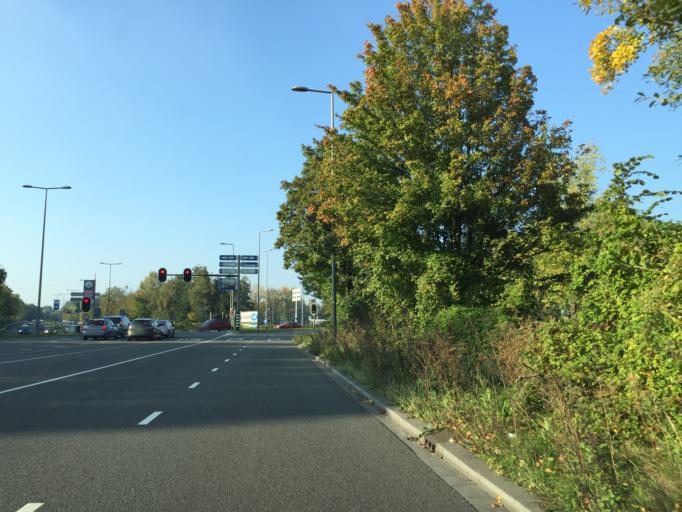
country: NL
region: South Holland
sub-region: Gemeente Barendrecht
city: Barendrecht
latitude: 51.8748
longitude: 4.5119
